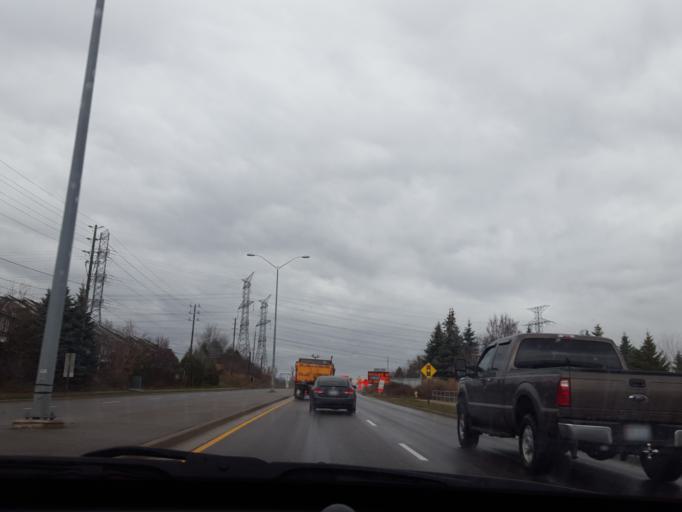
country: CA
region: Ontario
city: Ajax
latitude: 43.8649
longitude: -79.0819
